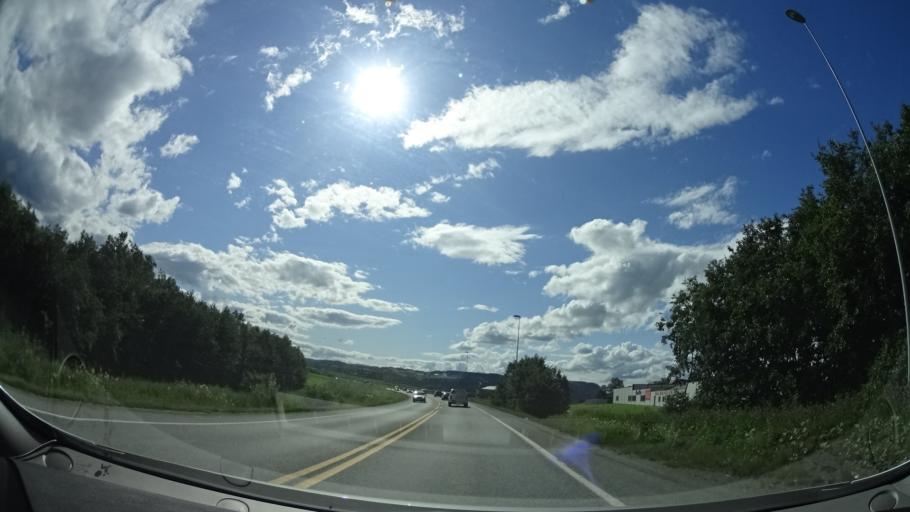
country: NO
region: Sor-Trondelag
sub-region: Melhus
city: Melhus
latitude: 63.3251
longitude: 10.3266
